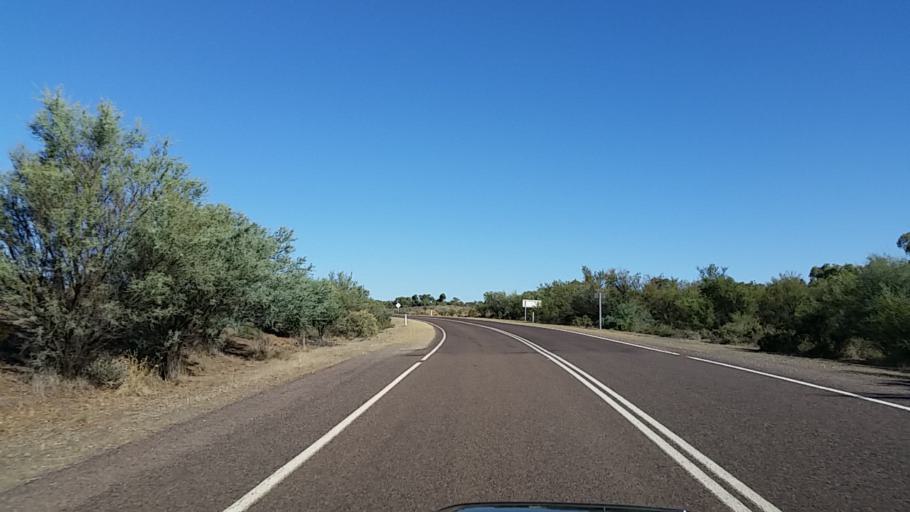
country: AU
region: South Australia
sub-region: Flinders Ranges
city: Quorn
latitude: -32.3331
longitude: 138.4739
